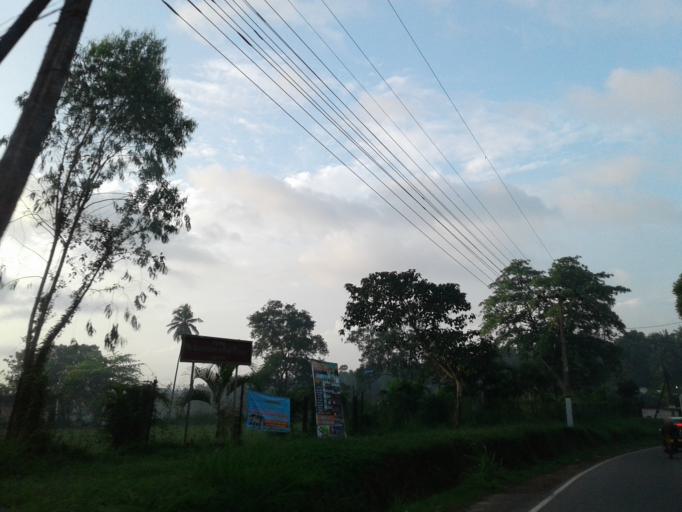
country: LK
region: Western
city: Kelaniya
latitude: 6.9807
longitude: 80.0093
